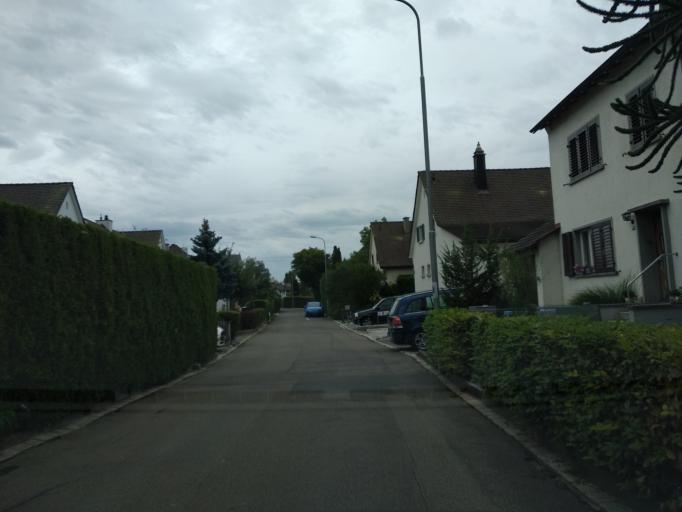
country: CH
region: Schaffhausen
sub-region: Bezirk Schaffhausen
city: Schaffhausen
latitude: 47.7146
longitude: 8.6474
